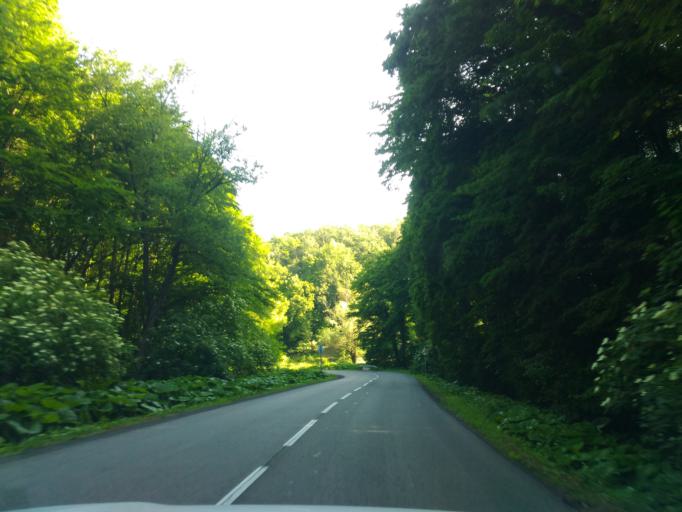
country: HU
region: Baranya
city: Komlo
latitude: 46.2111
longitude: 18.3016
